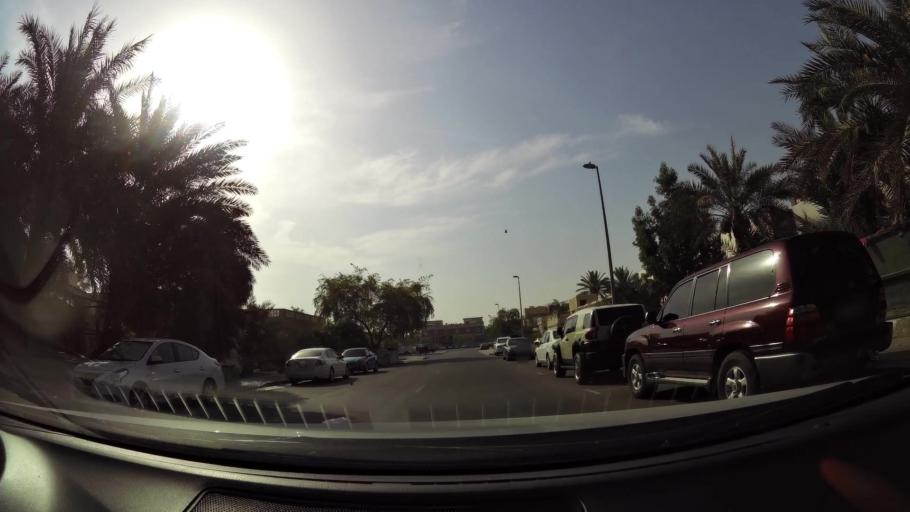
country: AE
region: Ash Shariqah
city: Sharjah
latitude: 25.2259
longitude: 55.3816
